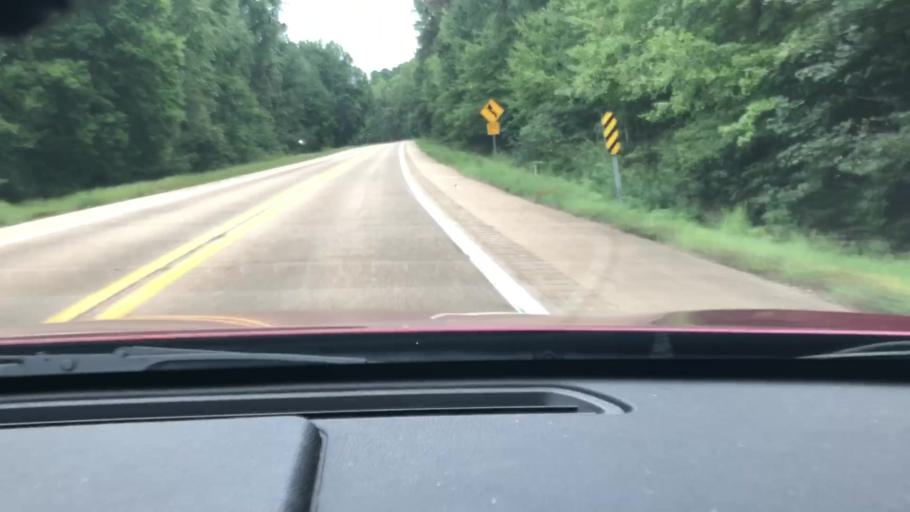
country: US
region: Arkansas
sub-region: Miller County
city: Texarkana
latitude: 33.4197
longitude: -93.8260
